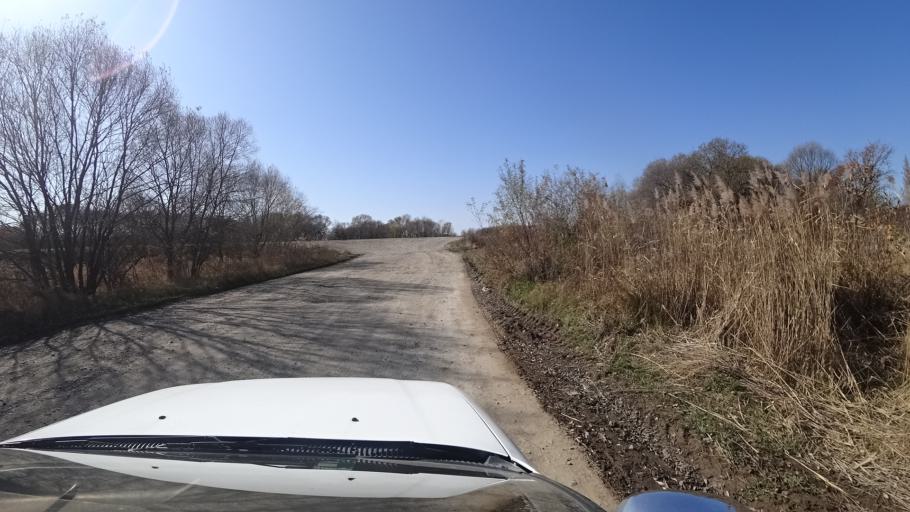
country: RU
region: Primorskiy
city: Dal'nerechensk
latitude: 45.9184
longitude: 133.7761
